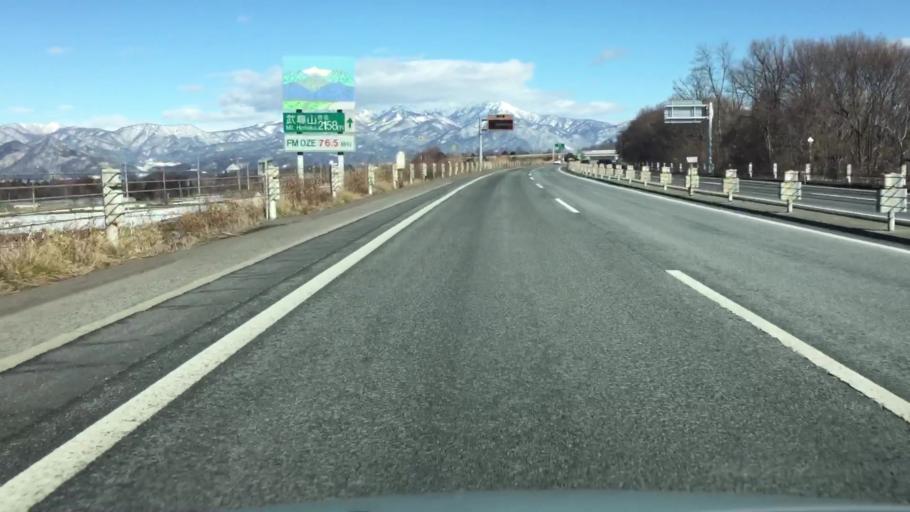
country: JP
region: Gunma
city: Numata
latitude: 36.6102
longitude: 139.0638
